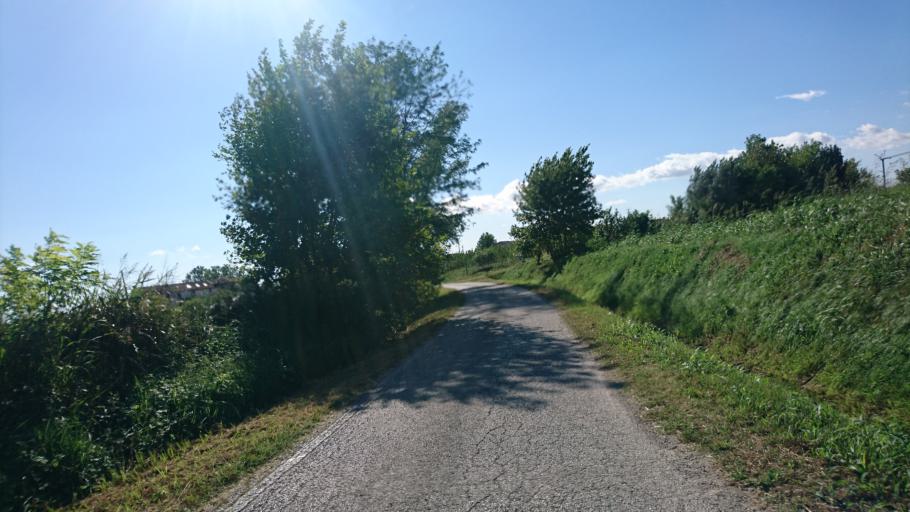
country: IT
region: Veneto
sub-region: Provincia di Venezia
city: Tombelle
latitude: 45.3997
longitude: 11.9880
